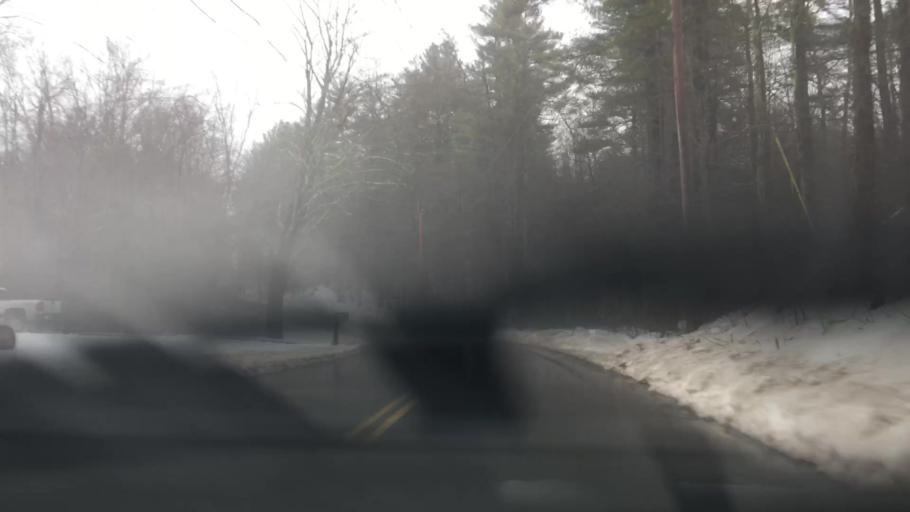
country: US
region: Massachusetts
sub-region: Hampshire County
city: Granby
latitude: 42.2581
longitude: -72.4626
